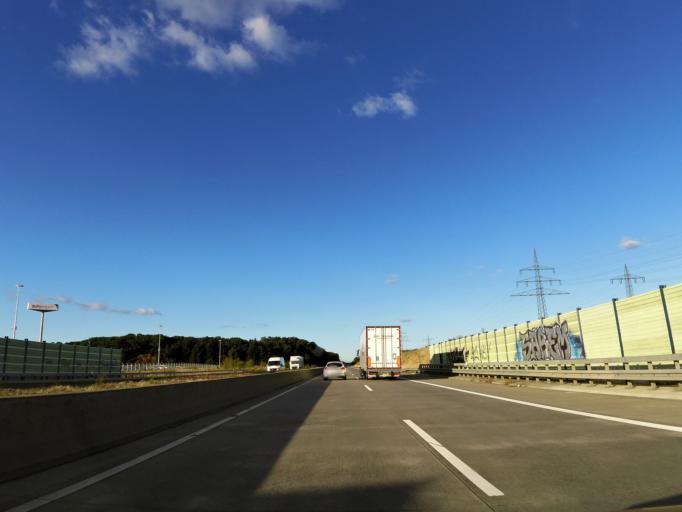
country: DE
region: Hesse
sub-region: Regierungsbezirk Giessen
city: Lich
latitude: 50.5548
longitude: 8.7888
